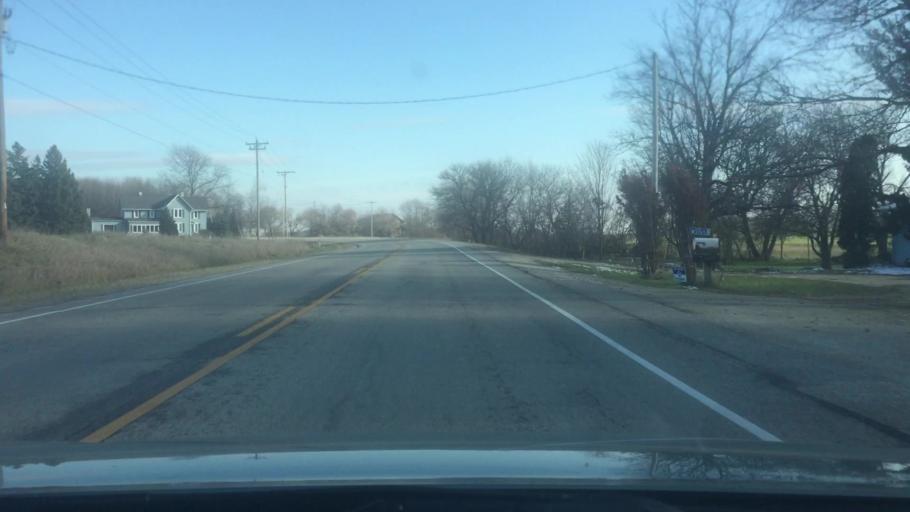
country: US
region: Wisconsin
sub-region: Walworth County
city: Whitewater
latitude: 42.9321
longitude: -88.7229
